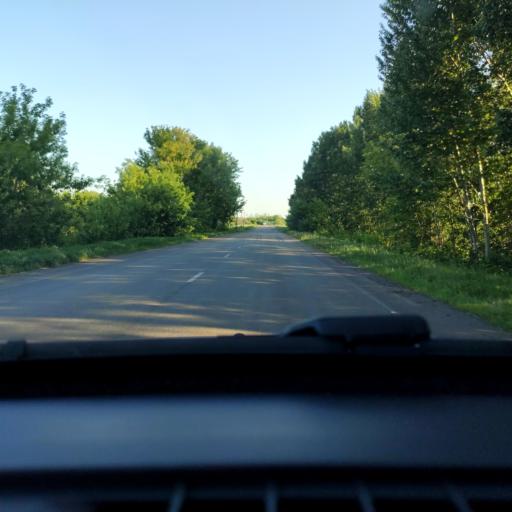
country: RU
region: Voronezj
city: Kashirskoye
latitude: 51.5089
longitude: 39.8324
